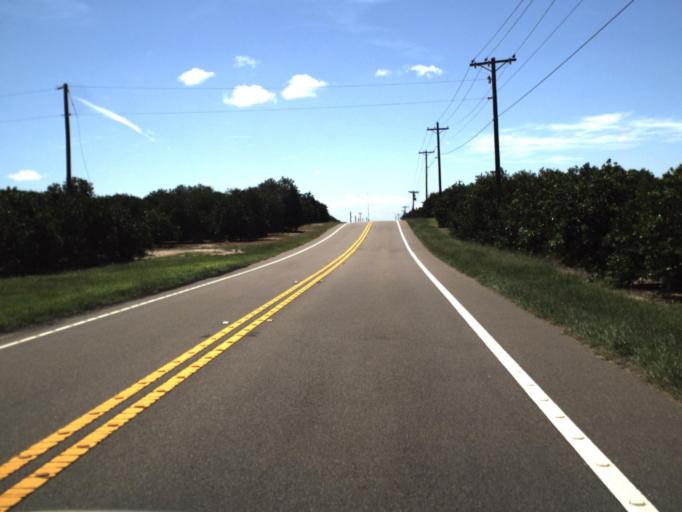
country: US
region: Florida
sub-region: Polk County
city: Babson Park
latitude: 27.7975
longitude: -81.5390
